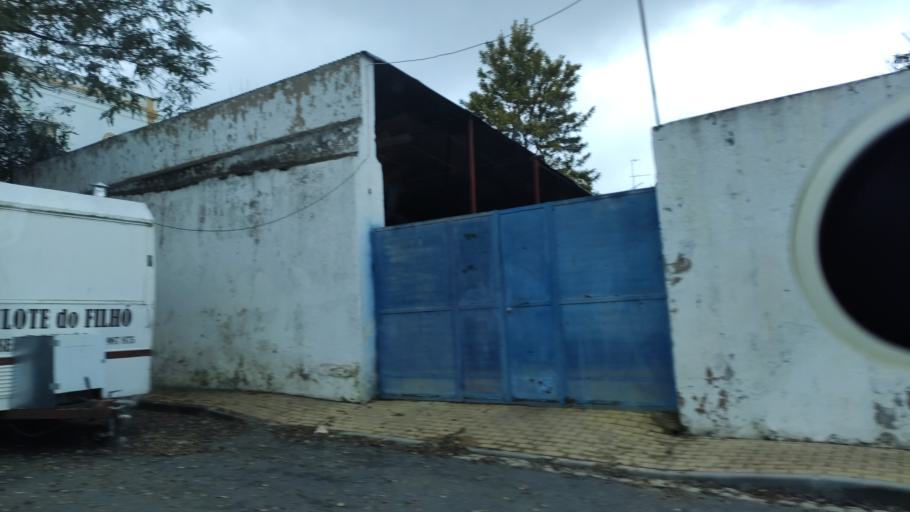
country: PT
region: Beja
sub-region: Beja
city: Beja
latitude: 38.0148
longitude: -7.8522
